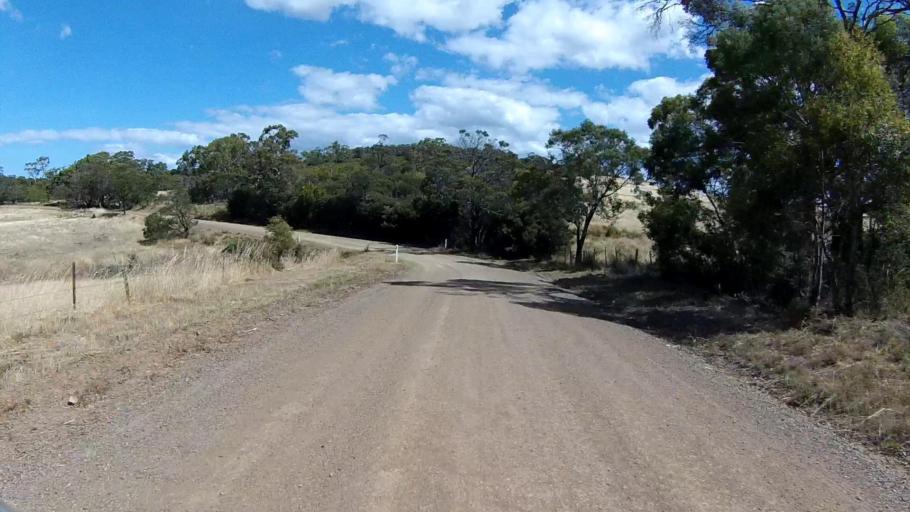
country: AU
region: Tasmania
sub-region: Break O'Day
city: St Helens
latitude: -41.9704
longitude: 148.0730
